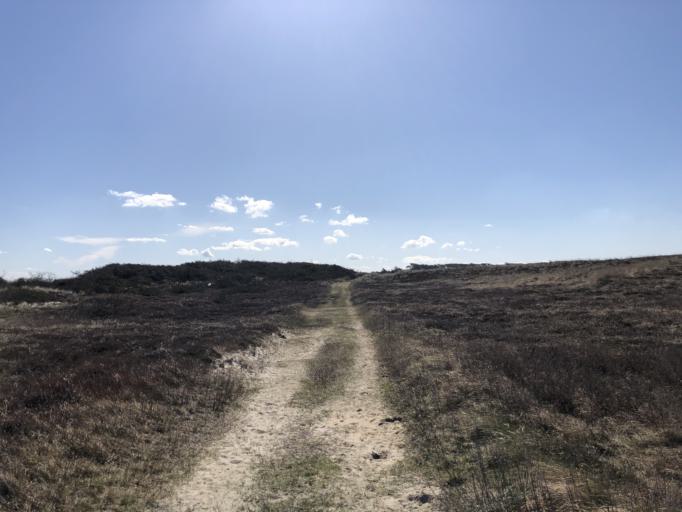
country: DK
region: Central Jutland
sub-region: Holstebro Kommune
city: Ulfborg
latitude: 56.3088
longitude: 8.1273
